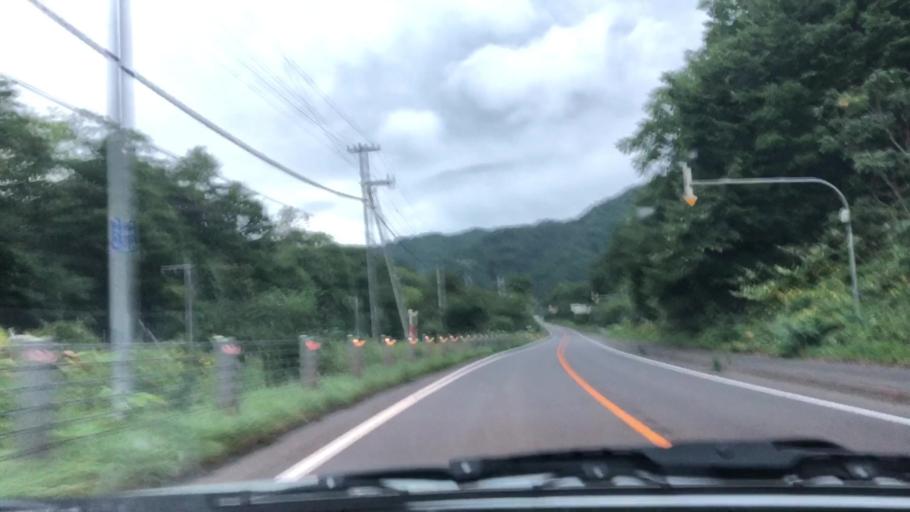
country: JP
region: Hokkaido
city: Chitose
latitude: 42.9138
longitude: 141.9652
